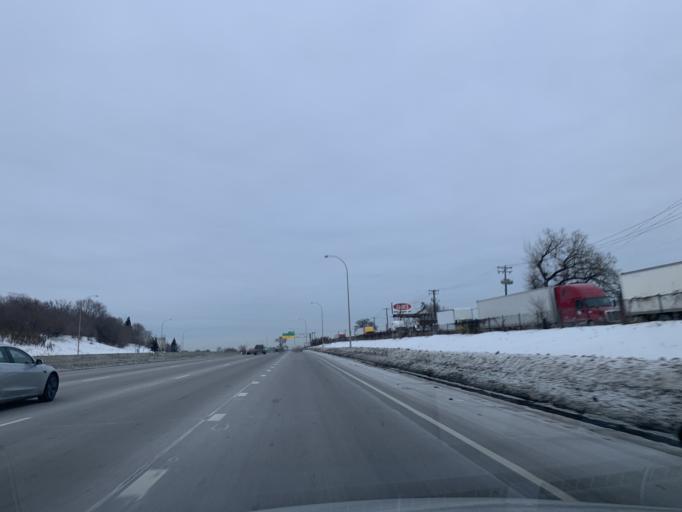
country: US
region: Minnesota
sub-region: Anoka County
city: Columbia Heights
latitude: 45.0167
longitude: -93.2823
